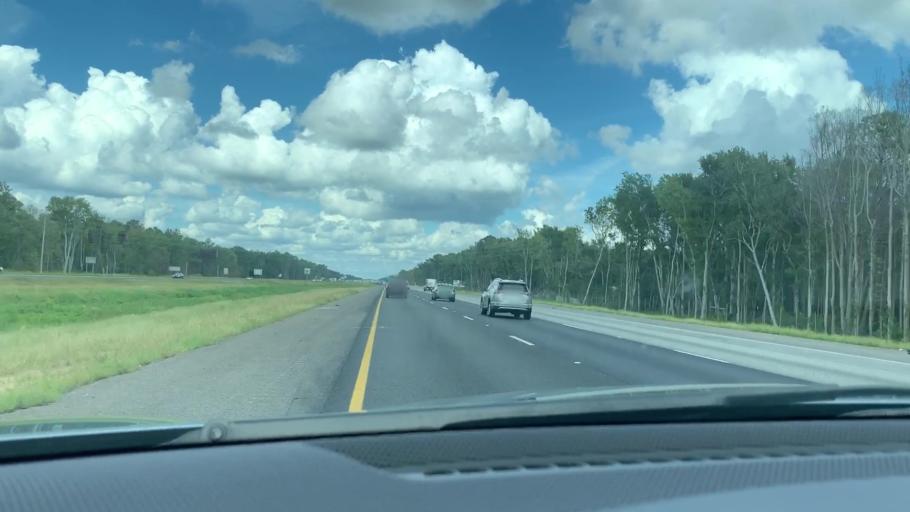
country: US
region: Georgia
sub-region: Camden County
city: Kingsland
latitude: 30.7971
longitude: -81.6600
